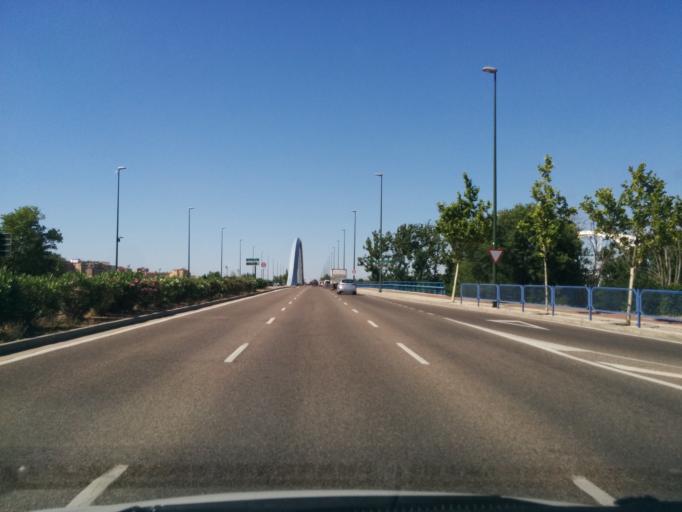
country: ES
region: Aragon
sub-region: Provincia de Zaragoza
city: Zaragoza
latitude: 41.6490
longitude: -0.8551
